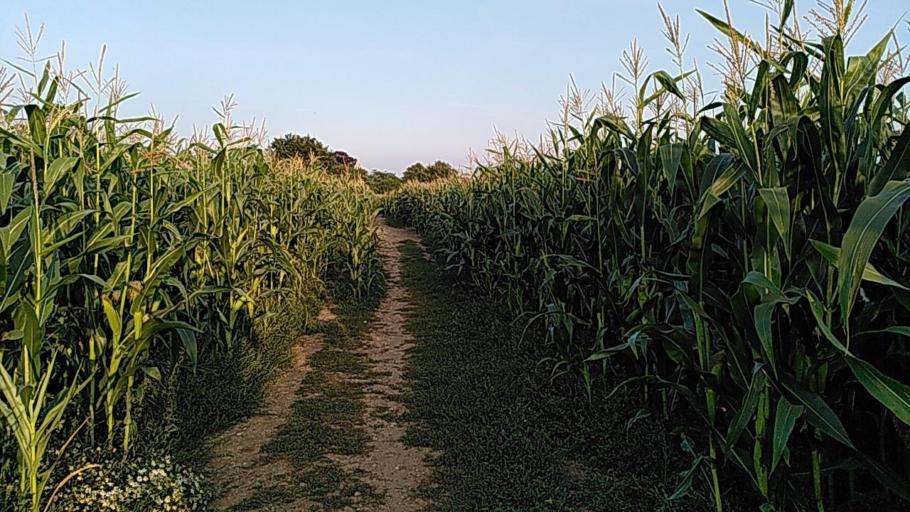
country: GB
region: England
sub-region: Oxfordshire
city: Sonning Common
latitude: 51.4921
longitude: -0.9495
